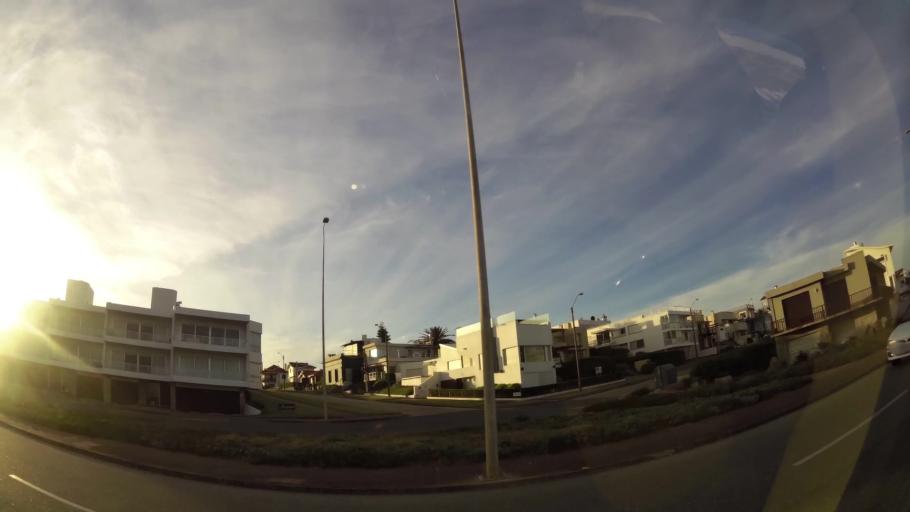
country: UY
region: Maldonado
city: Punta del Este
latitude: -34.9710
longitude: -54.9502
